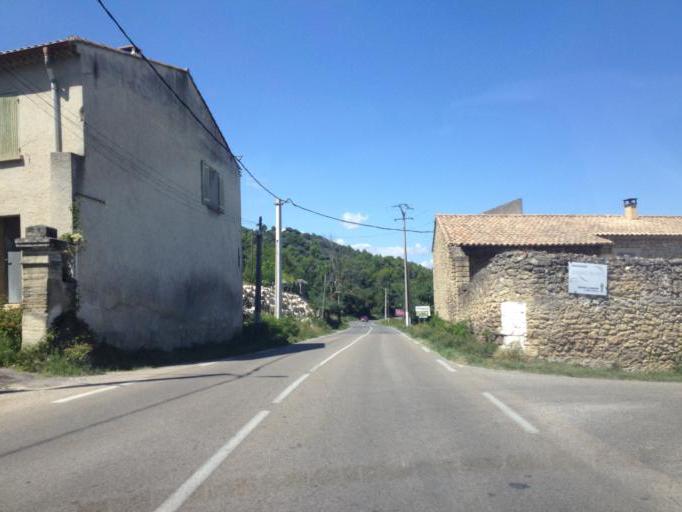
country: FR
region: Languedoc-Roussillon
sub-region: Departement du Gard
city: Sauveterre
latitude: 44.0112
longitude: 4.8004
